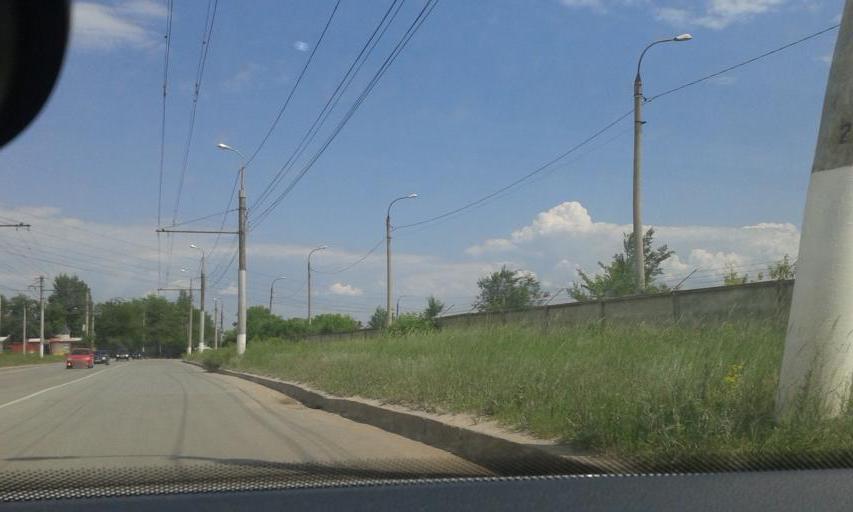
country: RU
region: Volgograd
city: Volgograd
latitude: 48.7558
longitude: 44.5136
